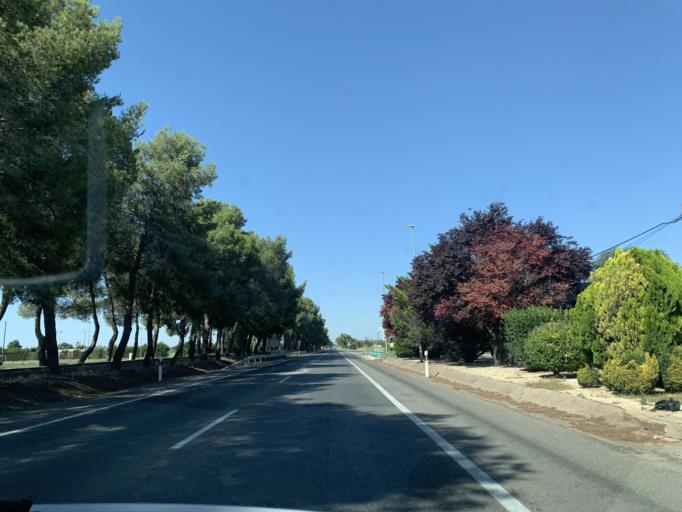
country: ES
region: Castille-La Mancha
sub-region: Provincia de Ciudad Real
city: Argamasilla de Alba
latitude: 39.1319
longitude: -3.0799
